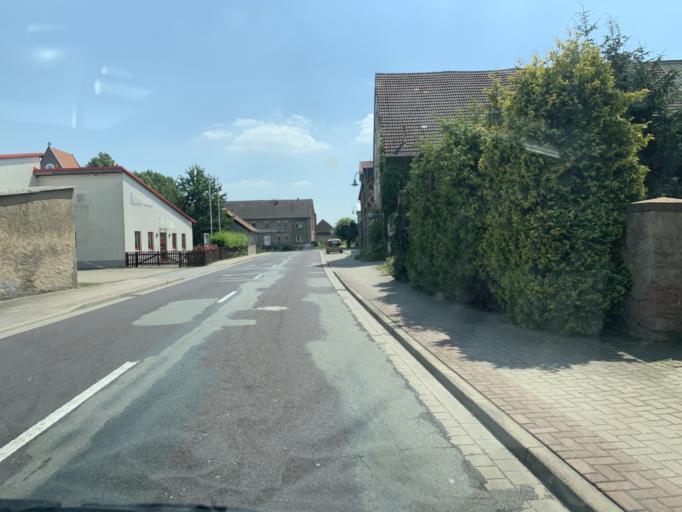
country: DE
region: Saxony-Anhalt
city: Erxleben
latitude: 52.2018
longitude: 11.2614
